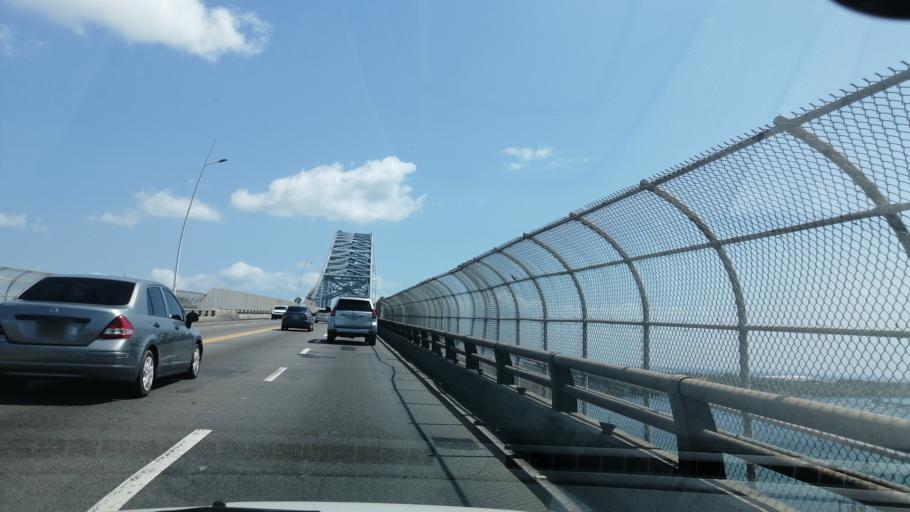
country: PA
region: Panama
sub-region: Distrito de Panama
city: Ancon
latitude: 8.9410
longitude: -79.5689
